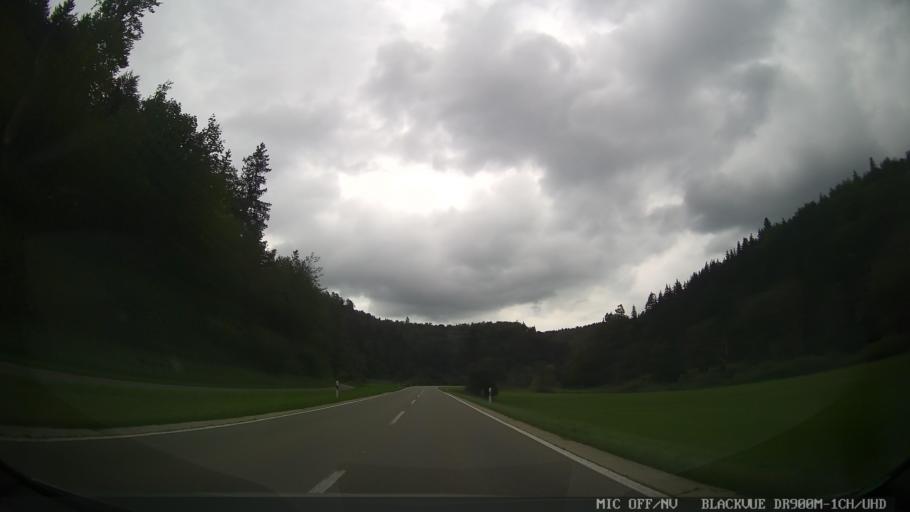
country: DE
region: Baden-Wuerttemberg
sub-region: Freiburg Region
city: Barenthal
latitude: 48.0545
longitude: 8.9314
